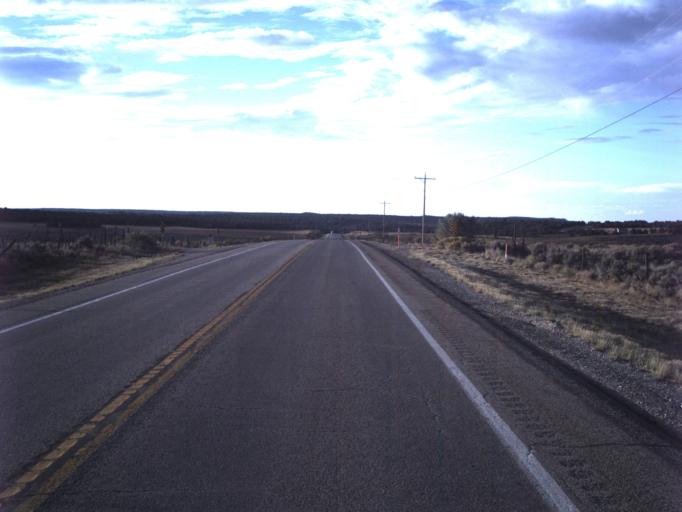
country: US
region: Utah
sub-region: San Juan County
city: Monticello
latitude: 37.9531
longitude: -109.3481
